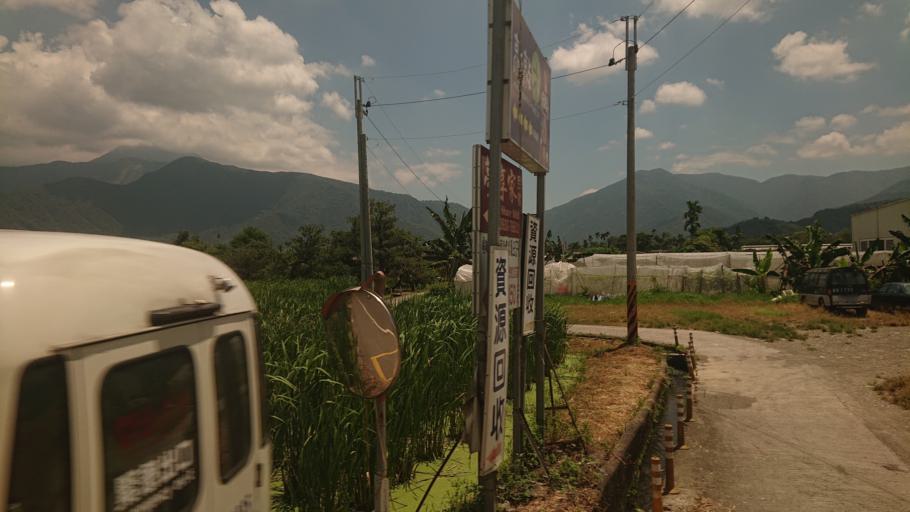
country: TW
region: Taiwan
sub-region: Nantou
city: Puli
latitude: 23.9764
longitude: 120.9619
